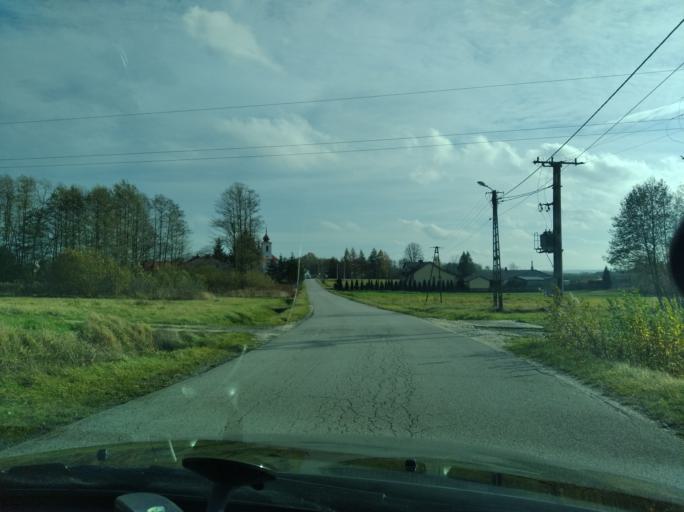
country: PL
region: Subcarpathian Voivodeship
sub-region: Powiat ropczycko-sedziszowski
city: Sedziszow Malopolski
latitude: 50.1170
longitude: 21.7307
